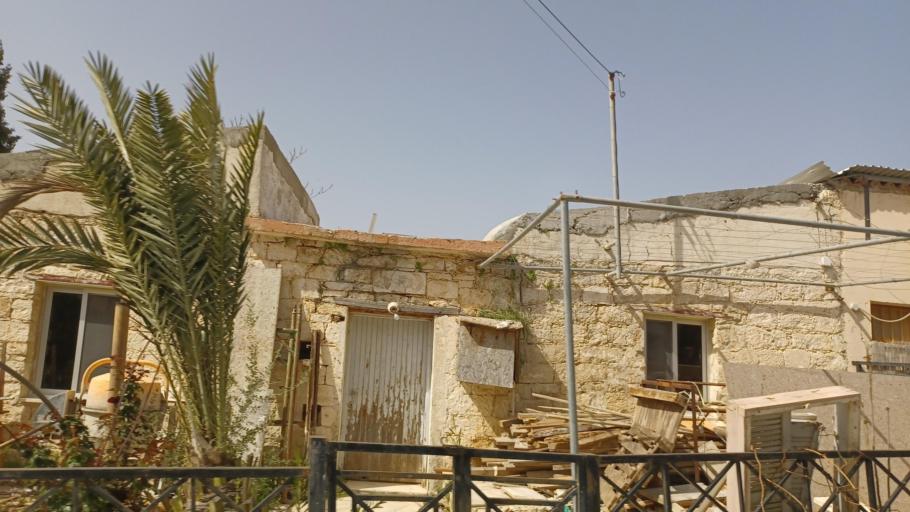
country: CY
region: Limassol
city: Pissouri
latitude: 34.7179
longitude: 32.7245
